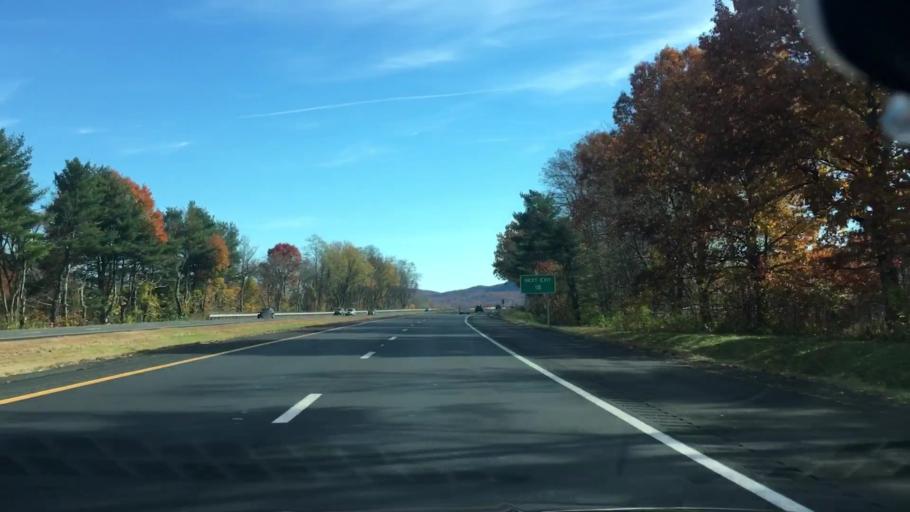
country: US
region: Massachusetts
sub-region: Hampshire County
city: Northampton
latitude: 42.3364
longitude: -72.6271
